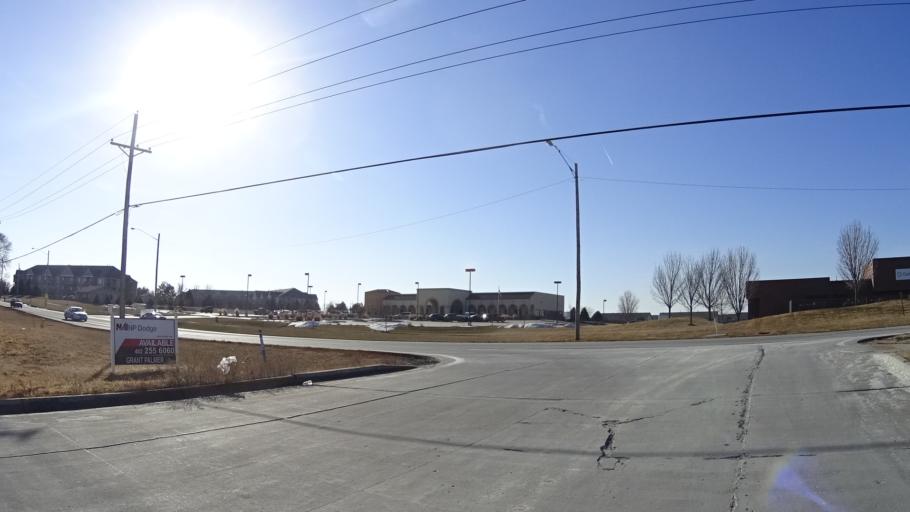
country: US
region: Nebraska
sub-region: Douglas County
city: Bennington
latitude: 41.3057
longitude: -96.1193
